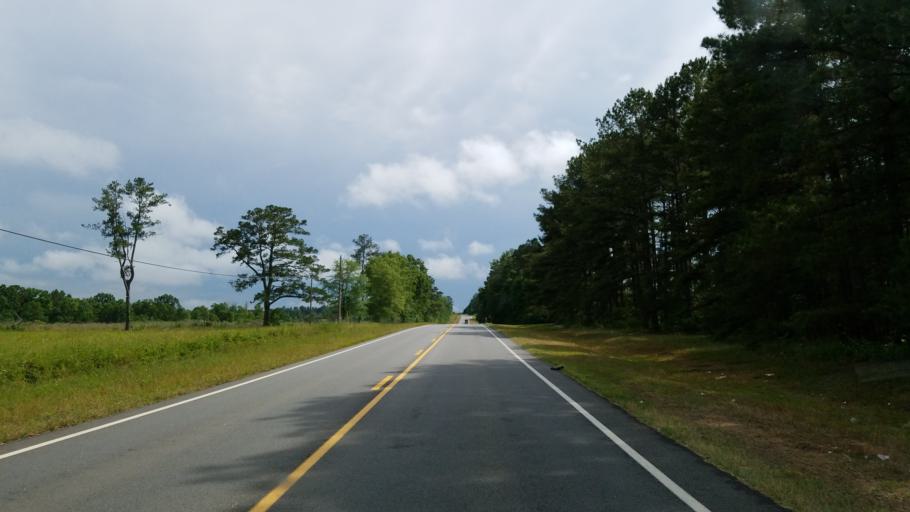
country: US
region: Georgia
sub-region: Houston County
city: Perry
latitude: 32.3991
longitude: -83.7841
